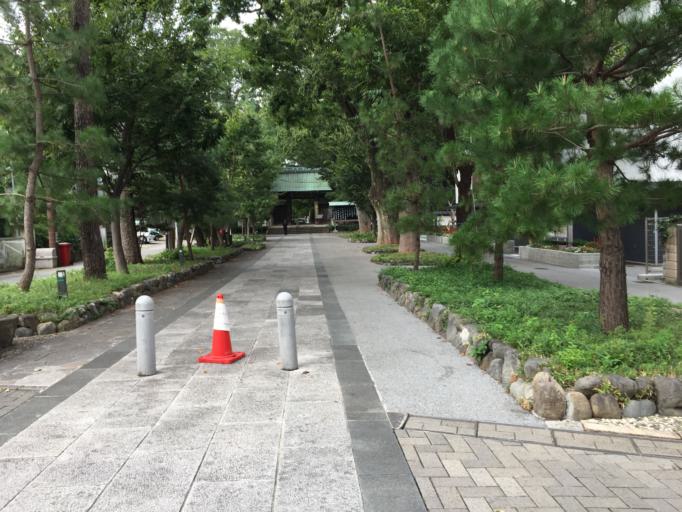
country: JP
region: Tokyo
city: Tokyo
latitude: 35.6067
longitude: 139.6617
